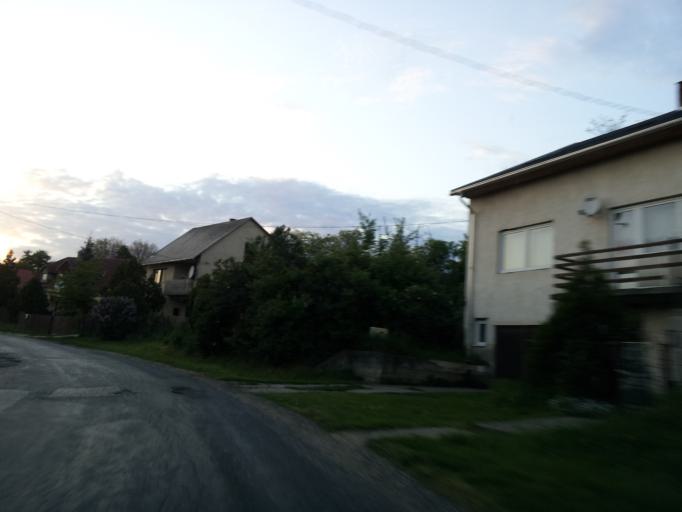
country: HU
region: Pest
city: Perbal
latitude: 47.6424
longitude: 18.7457
